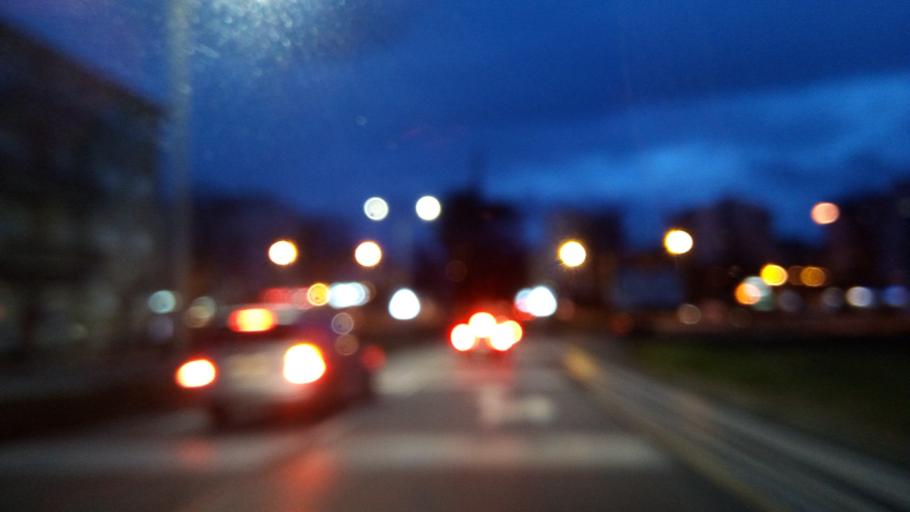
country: PT
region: Viseu
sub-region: Viseu
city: Viseu
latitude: 40.6501
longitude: -7.9126
